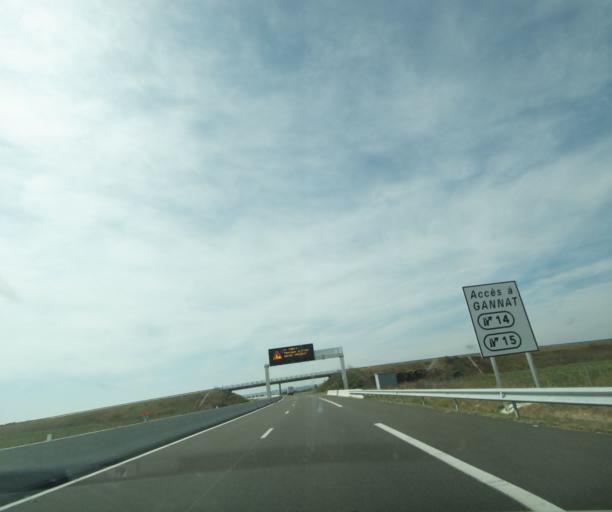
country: FR
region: Auvergne
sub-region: Departement de l'Allier
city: Brout-Vernet
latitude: 46.1147
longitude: 3.2761
